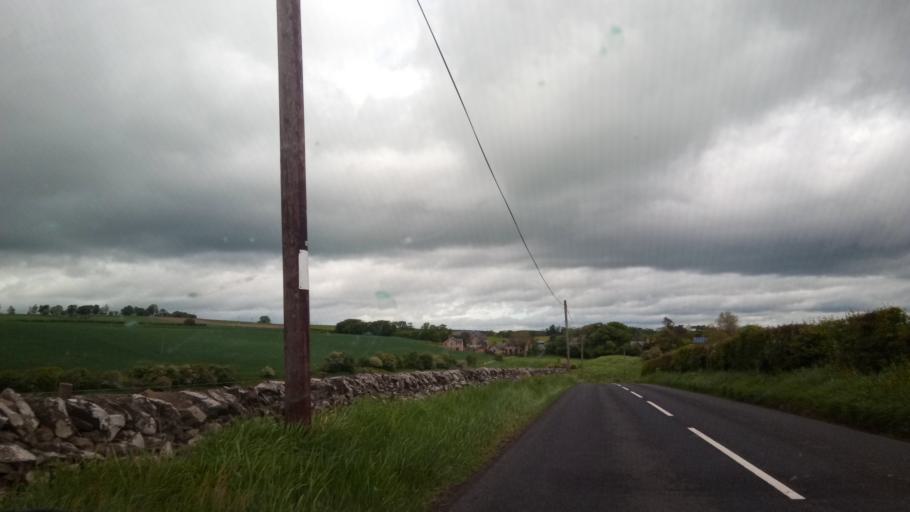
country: GB
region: Scotland
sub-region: The Scottish Borders
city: Hawick
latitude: 55.4535
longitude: -2.7557
